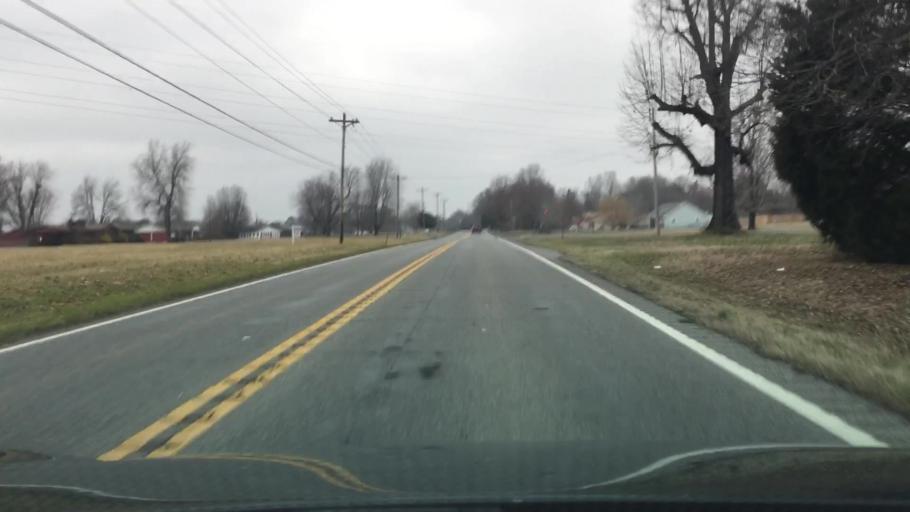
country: US
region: Kentucky
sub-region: Marshall County
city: Calvert City
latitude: 36.9523
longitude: -88.3697
